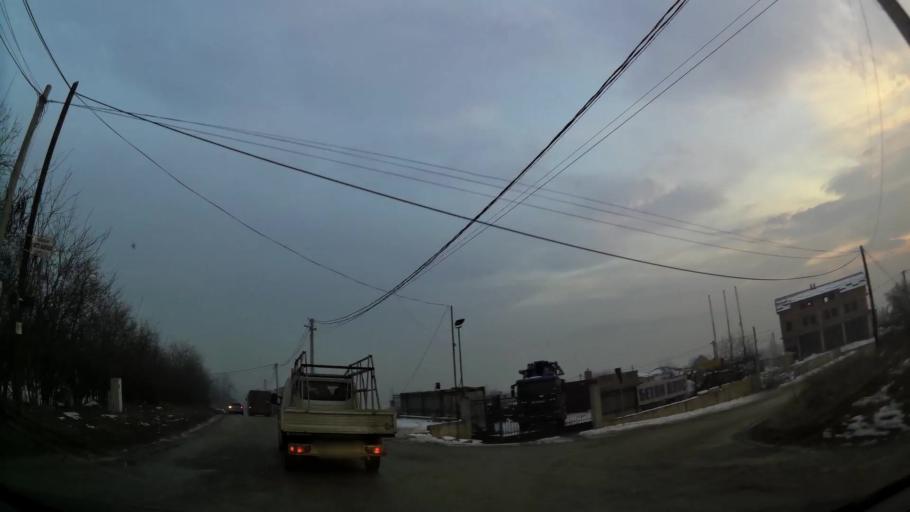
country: MK
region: Suto Orizari
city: Suto Orizare
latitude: 42.0300
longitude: 21.4070
